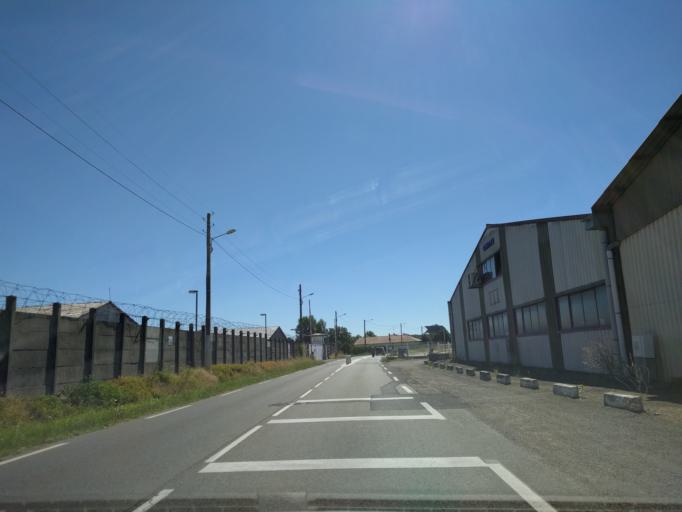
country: FR
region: Midi-Pyrenees
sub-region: Departement du Tarn-et-Garonne
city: Montauban
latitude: 44.0288
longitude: 1.3772
